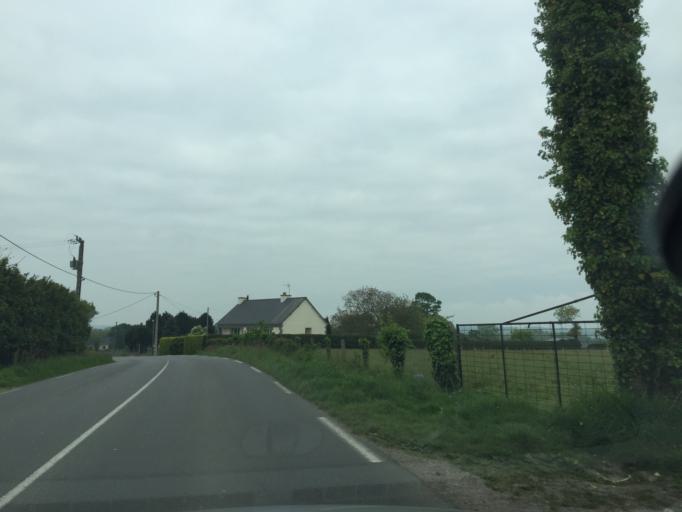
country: FR
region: Brittany
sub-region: Departement des Cotes-d'Armor
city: Matignon
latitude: 48.5884
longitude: -2.3153
